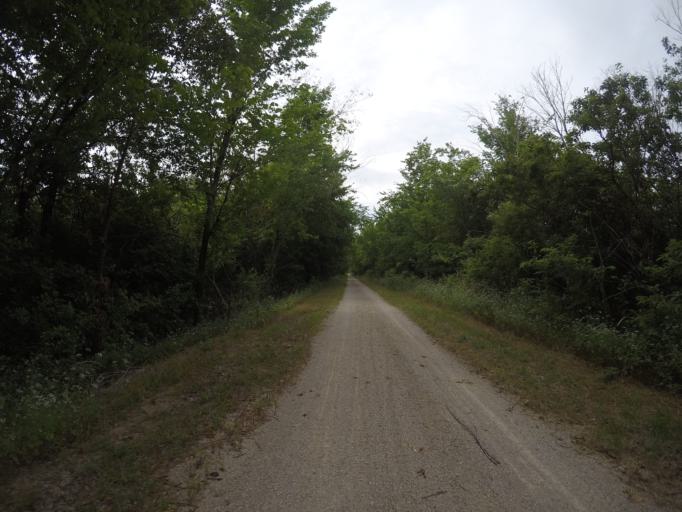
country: US
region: Kansas
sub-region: Franklin County
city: Ottawa
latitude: 38.5295
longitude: -95.2721
